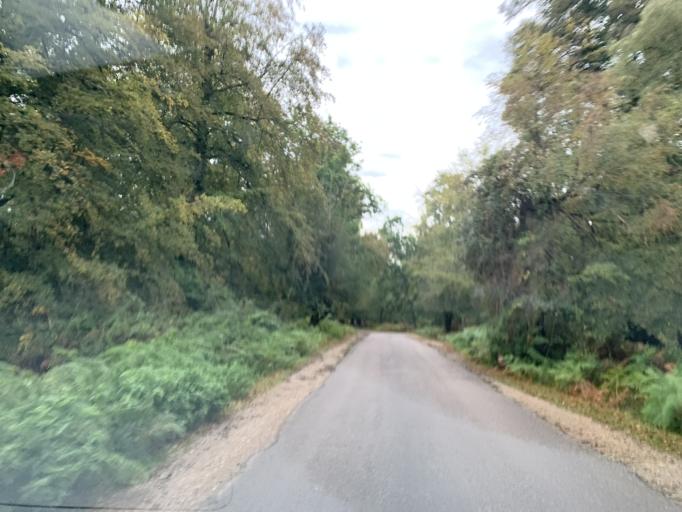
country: GB
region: England
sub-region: Hampshire
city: Lyndhurst
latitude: 50.8616
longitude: -1.6466
